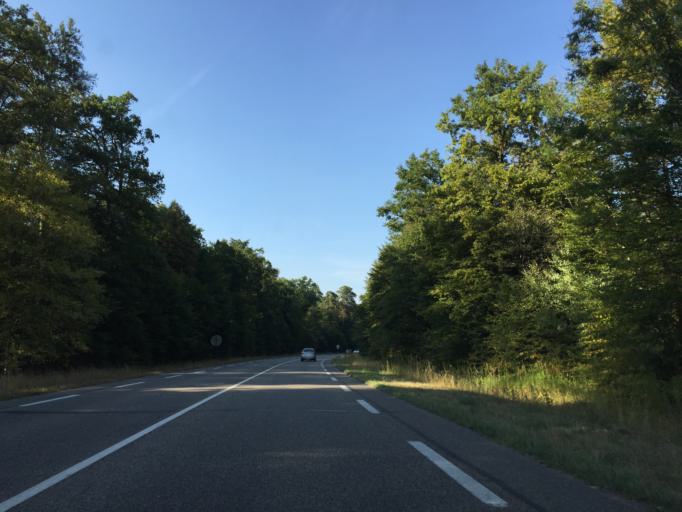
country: FR
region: Alsace
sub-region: Departement du Bas-Rhin
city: Haguenau
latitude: 48.8430
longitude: 7.8059
